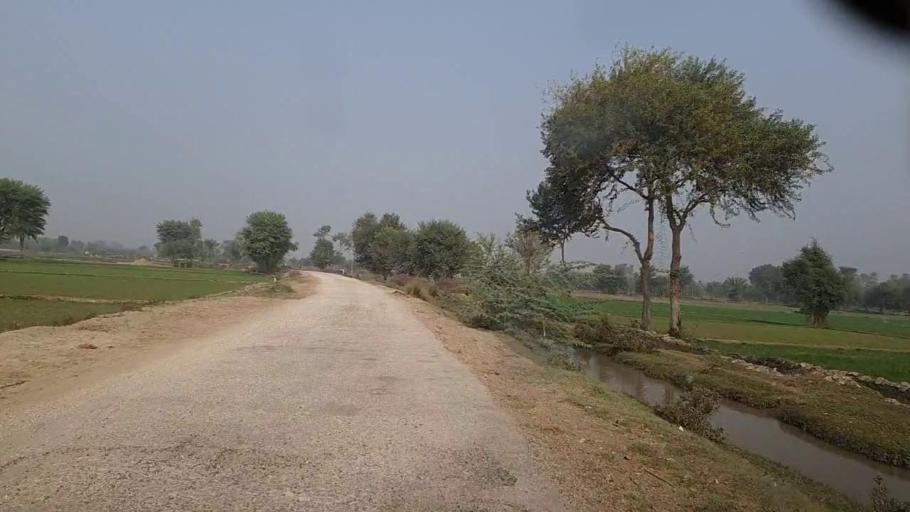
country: PK
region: Sindh
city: Bozdar
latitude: 27.0653
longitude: 68.6371
